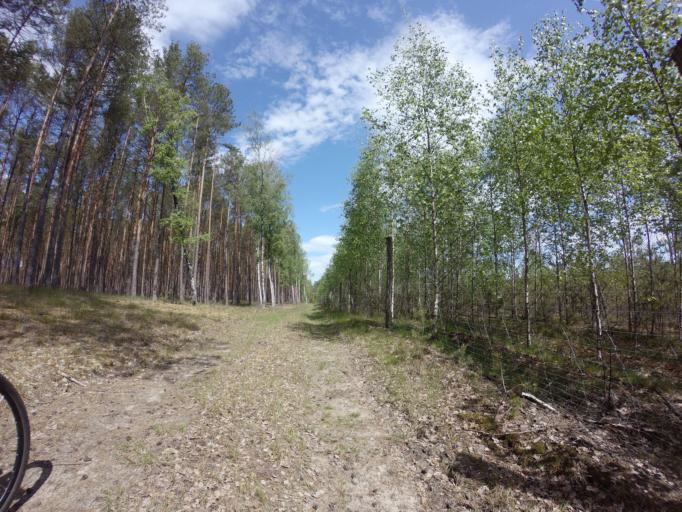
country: PL
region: West Pomeranian Voivodeship
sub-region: Powiat drawski
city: Kalisz Pomorski
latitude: 53.1900
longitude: 15.9634
